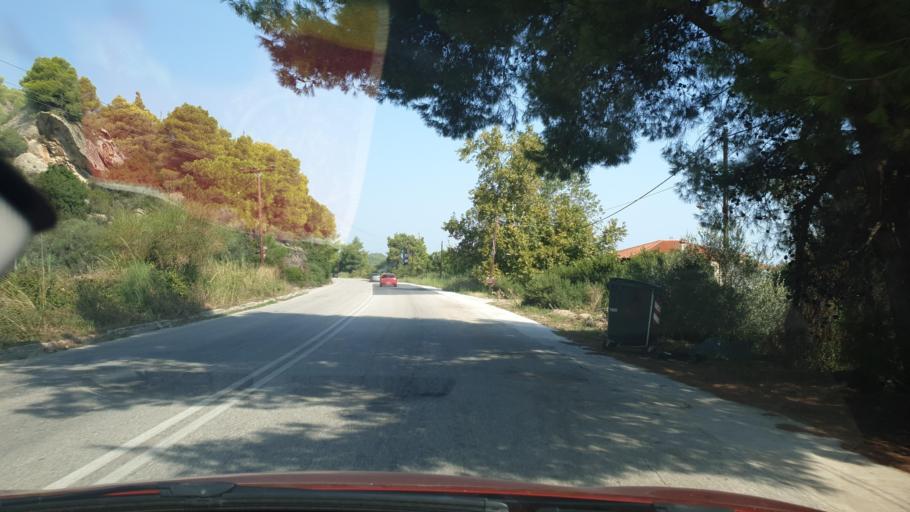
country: GR
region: Central Macedonia
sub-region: Nomos Chalkidikis
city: Agios Nikolaos
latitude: 40.1964
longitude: 23.7680
